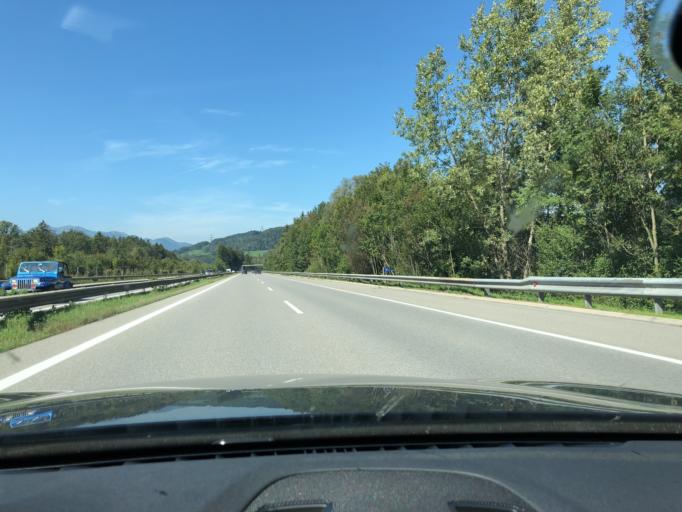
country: AT
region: Vorarlberg
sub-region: Politischer Bezirk Feldkirch
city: Satteins
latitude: 47.2112
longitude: 9.6643
